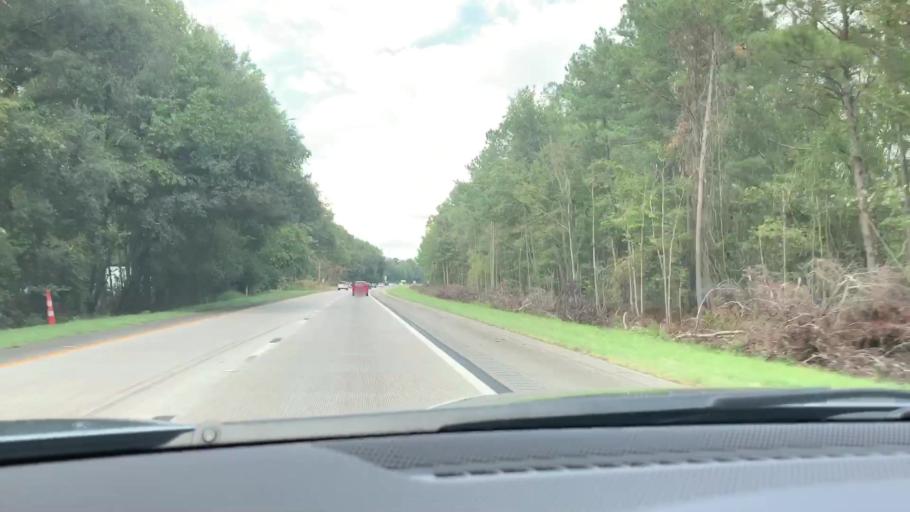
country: US
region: South Carolina
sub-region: Jasper County
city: Ridgeland
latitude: 32.4144
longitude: -81.0121
